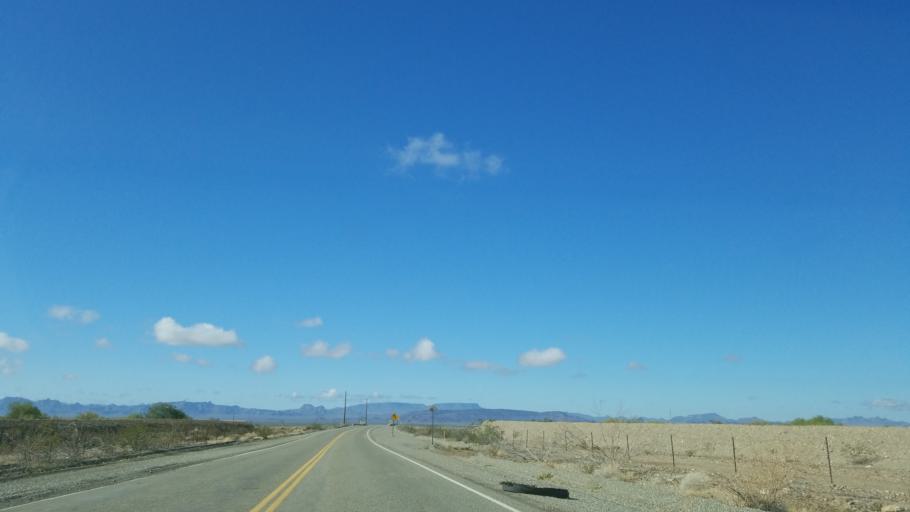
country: US
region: Arizona
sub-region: La Paz County
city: Salome
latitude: 33.7409
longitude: -113.7546
